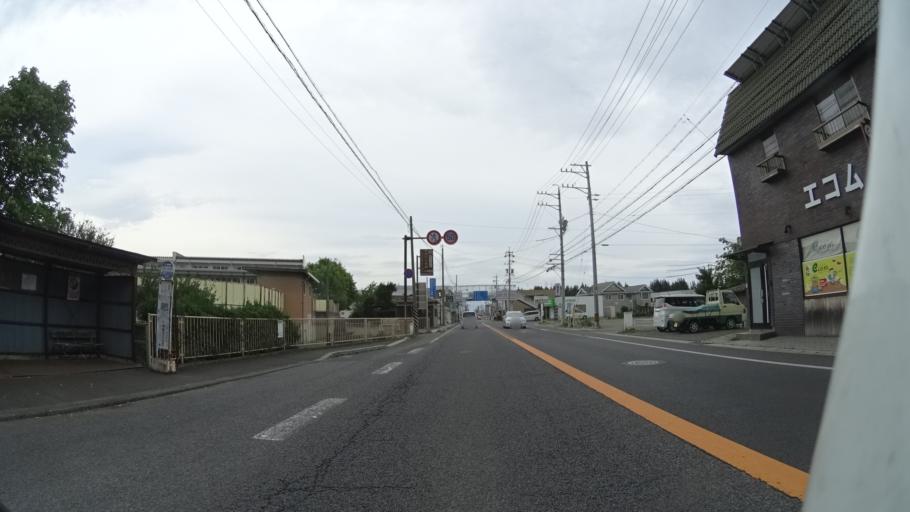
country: JP
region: Nagano
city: Nagano-shi
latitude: 36.5911
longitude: 138.1545
